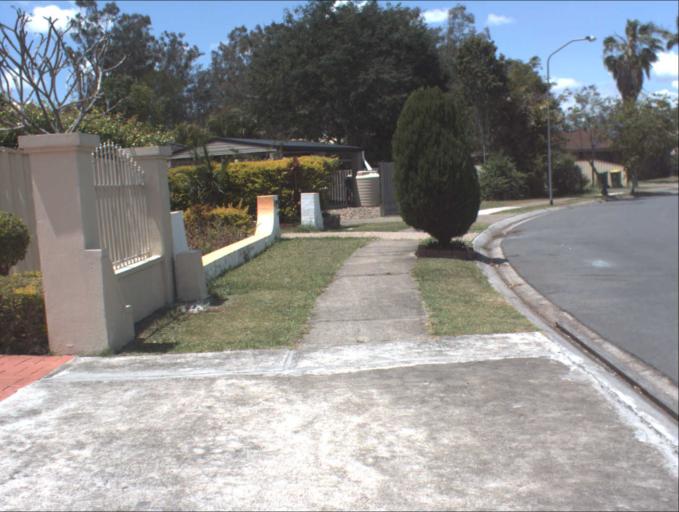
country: AU
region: Queensland
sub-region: Logan
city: Slacks Creek
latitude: -27.6663
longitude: 153.1425
